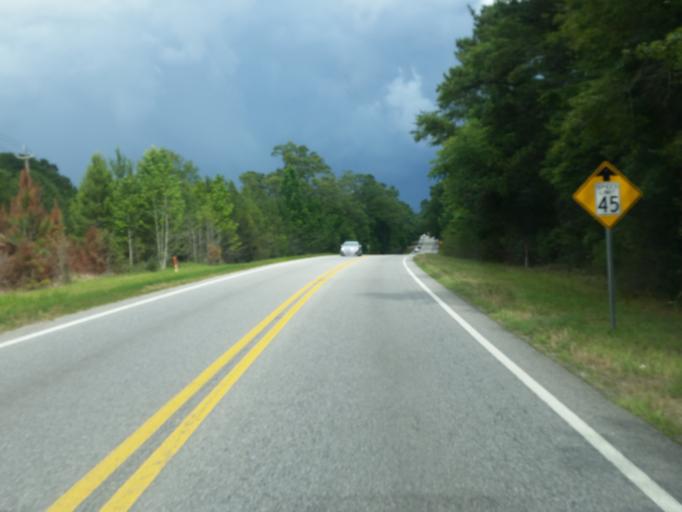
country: US
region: Mississippi
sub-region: Jackson County
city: Hurley
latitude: 30.8255
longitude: -88.3682
